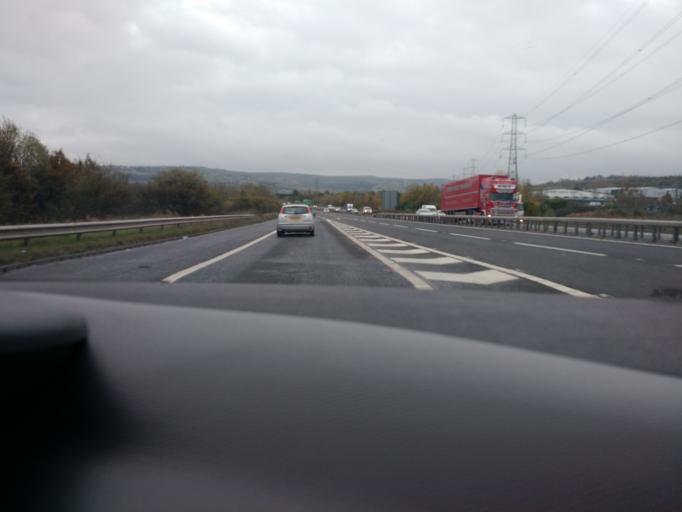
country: GB
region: England
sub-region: Blackburn with Darwen
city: Darwen
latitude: 53.7161
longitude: -2.4744
